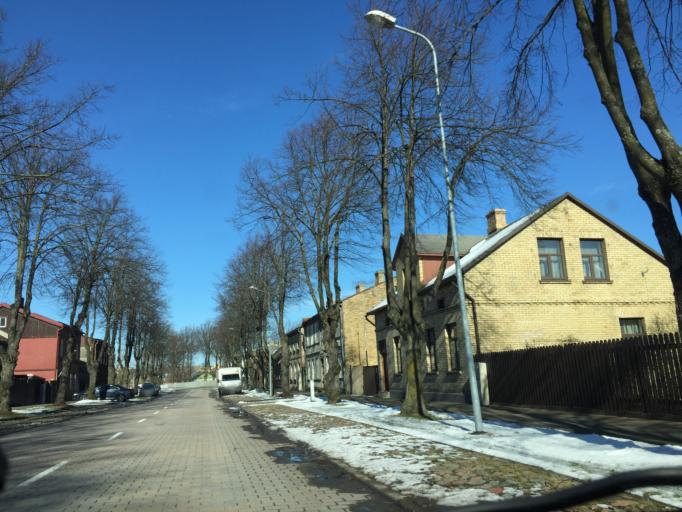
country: LV
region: Ventspils
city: Ventspils
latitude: 57.3909
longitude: 21.5546
